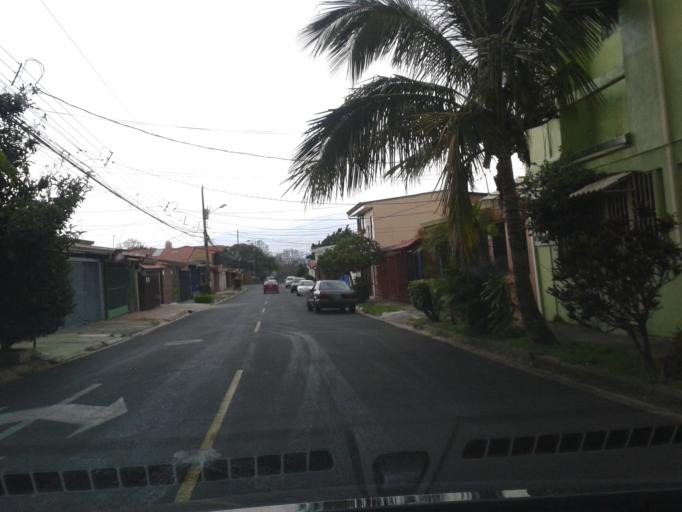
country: CR
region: Heredia
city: San Francisco
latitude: 9.9915
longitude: -84.1285
